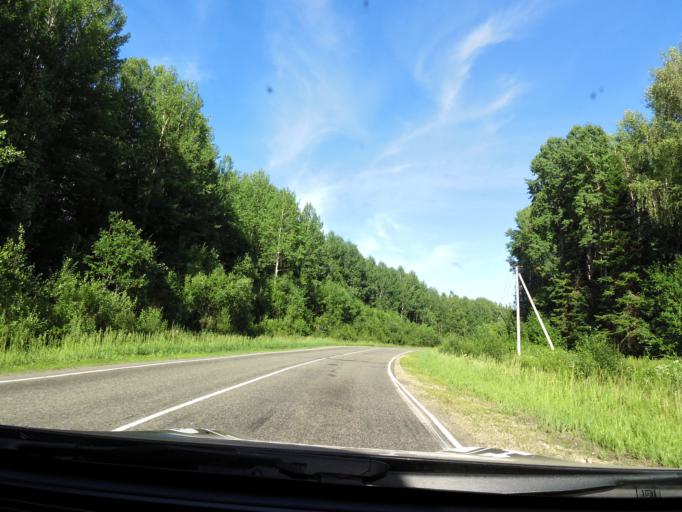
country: RU
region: Kirov
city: Belaya Kholunitsa
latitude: 58.9208
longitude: 51.1152
